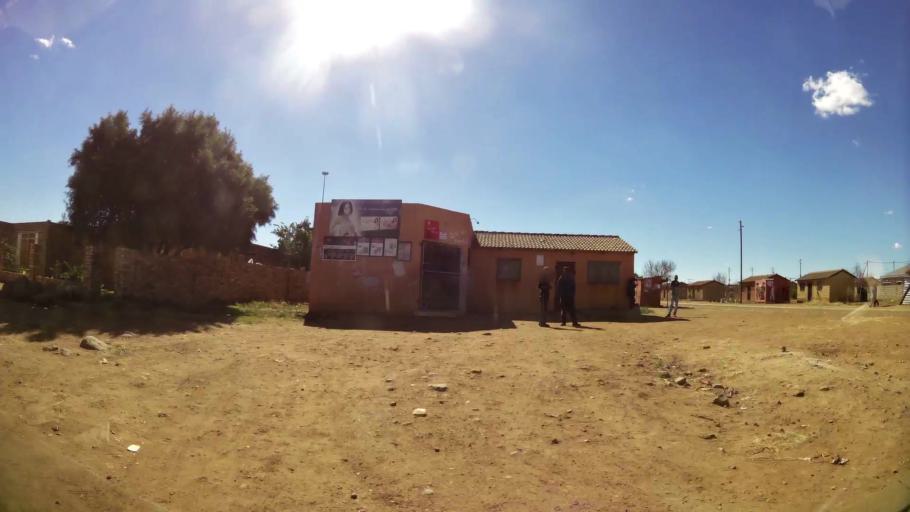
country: ZA
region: North-West
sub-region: Dr Kenneth Kaunda District Municipality
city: Klerksdorp
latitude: -26.8741
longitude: 26.5694
